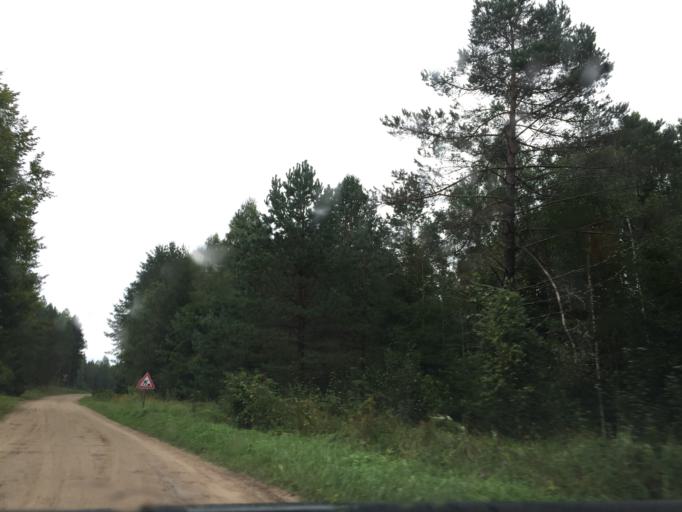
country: LV
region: Preilu Rajons
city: Jaunaglona
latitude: 56.2566
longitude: 27.1383
